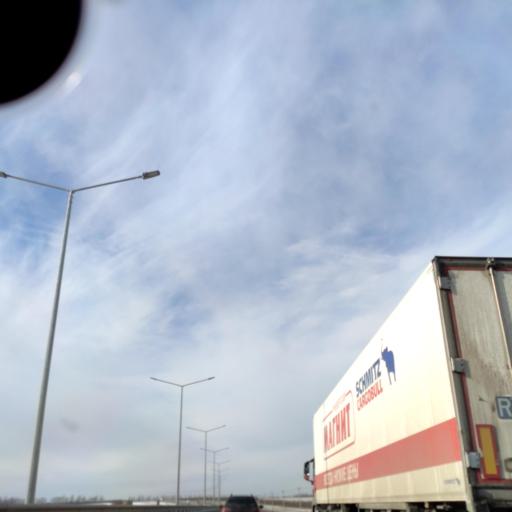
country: RU
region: Voronezj
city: Podkletnoye
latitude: 51.5816
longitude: 39.4601
